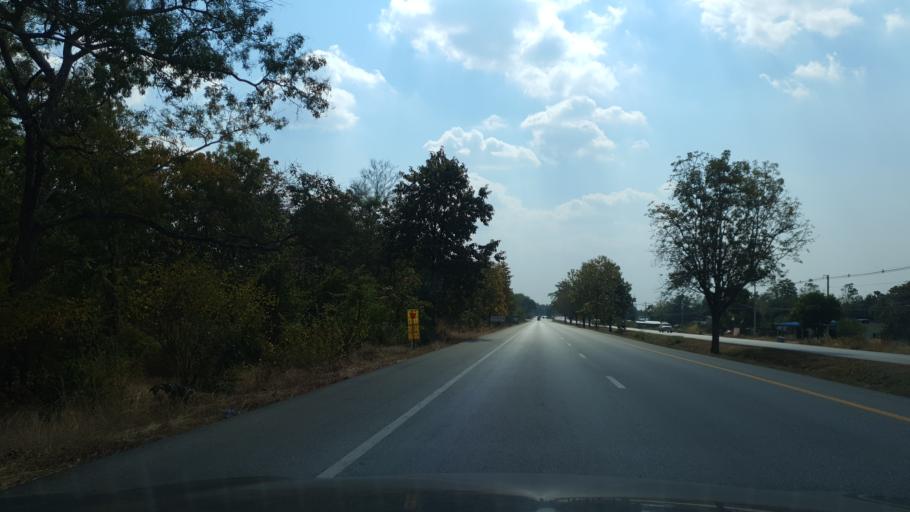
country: TH
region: Tak
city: Sam Ngao
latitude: 17.2912
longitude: 99.1424
